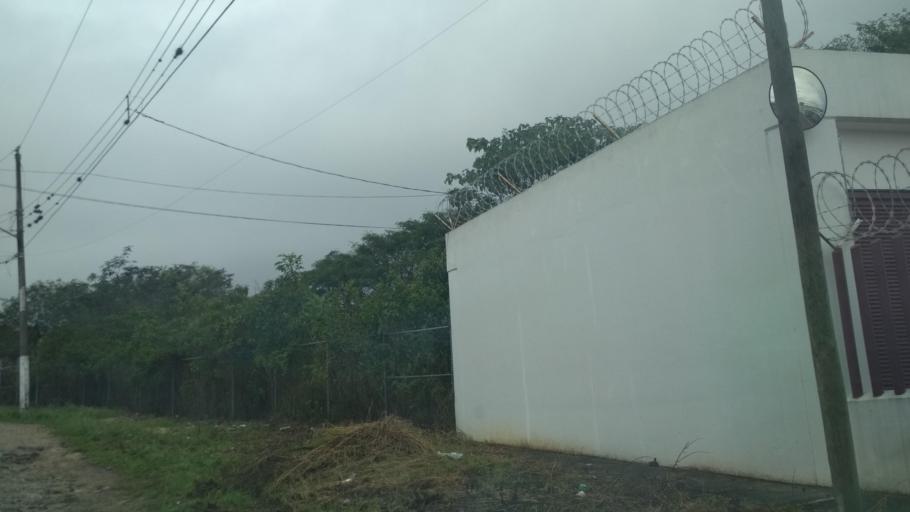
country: MX
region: Veracruz
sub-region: Xalapa
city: Colonia Santa Barbara
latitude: 19.5072
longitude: -96.8747
